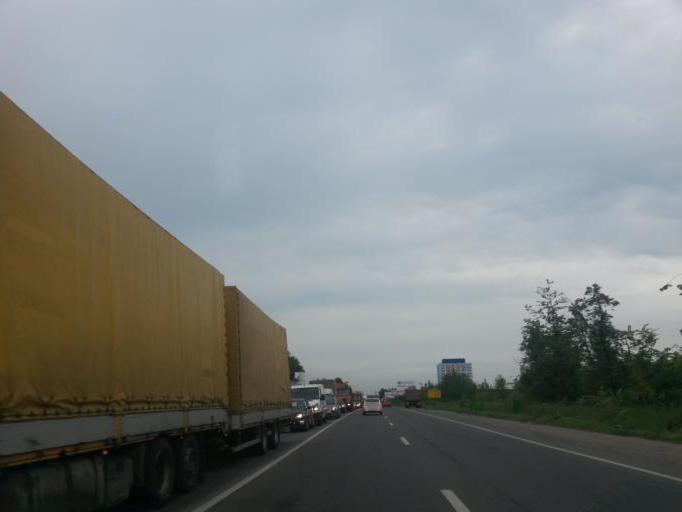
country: RU
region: Moskovskaya
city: Petrovskaya
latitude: 55.5536
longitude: 37.7749
